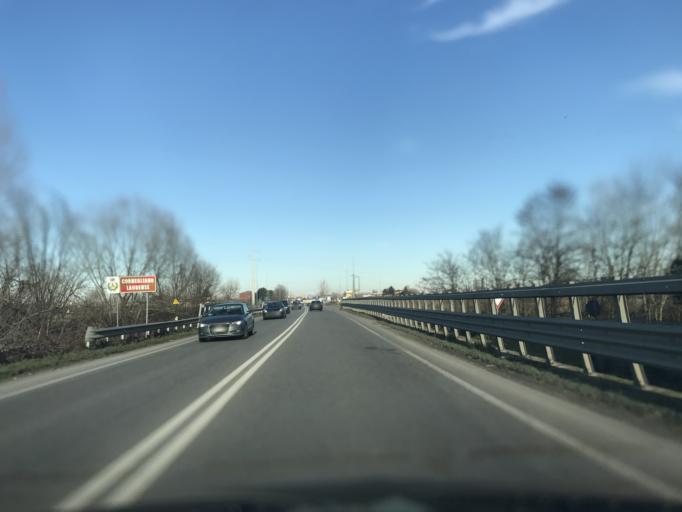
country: IT
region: Lombardy
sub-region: Provincia di Lodi
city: Muzza di Cornegliano Laudense
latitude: 45.2927
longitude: 9.4763
